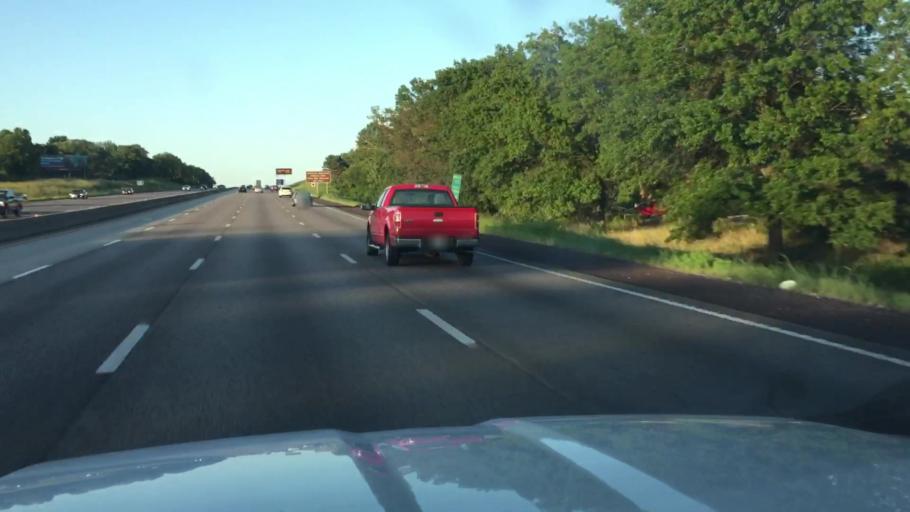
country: US
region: Missouri
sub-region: Saint Louis County
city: Saint George
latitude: 38.5256
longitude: -90.3186
